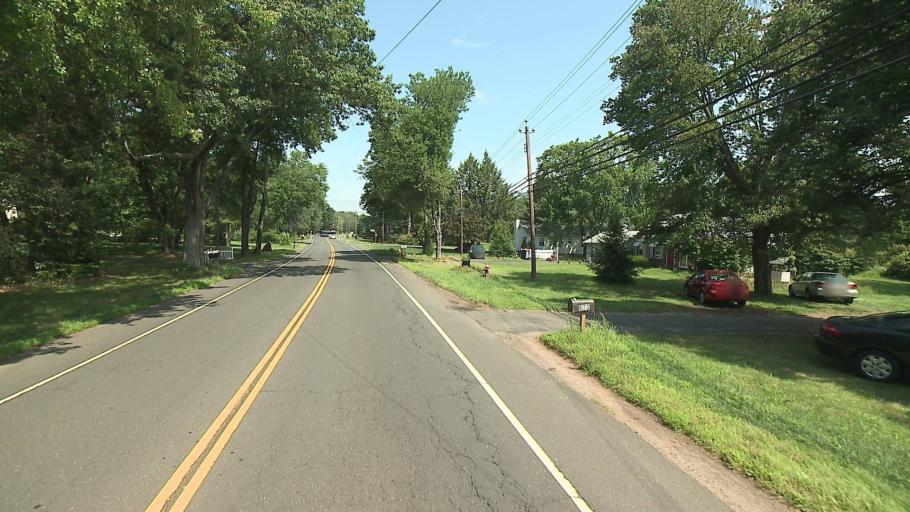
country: US
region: Connecticut
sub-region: Hartford County
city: Plainville
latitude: 41.7010
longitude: -72.8782
